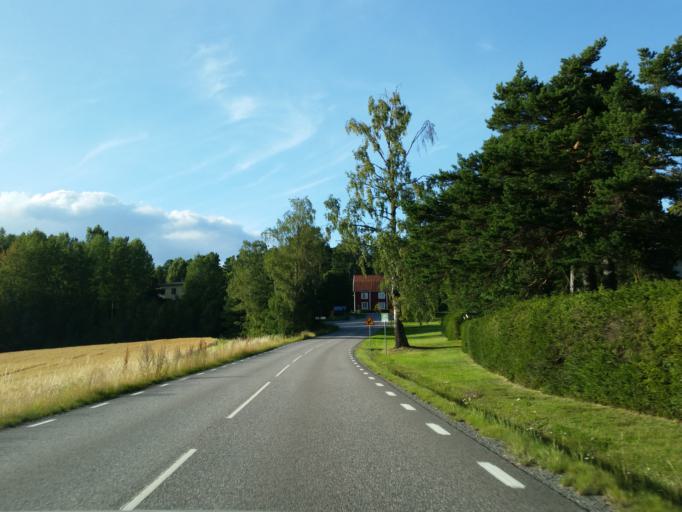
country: SE
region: Soedermanland
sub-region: Gnesta Kommun
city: Gnesta
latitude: 59.0281
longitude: 17.3580
